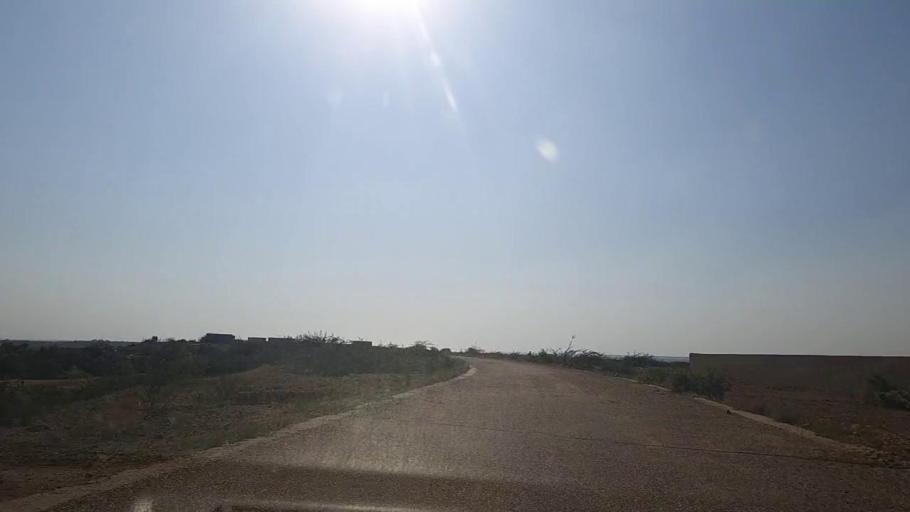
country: PK
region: Sindh
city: Daro Mehar
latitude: 25.0057
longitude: 68.1158
